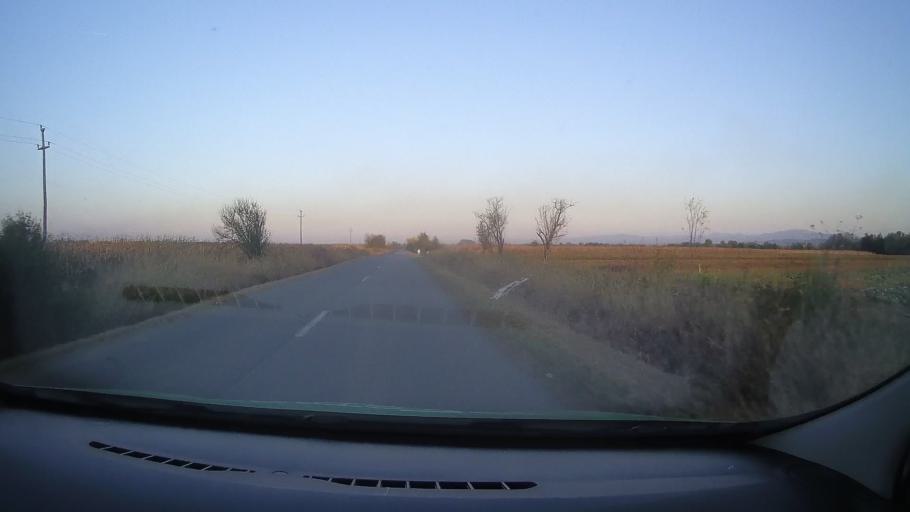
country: RO
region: Timis
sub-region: Comuna Manastiur
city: Manastiur
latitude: 45.8351
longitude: 22.0372
